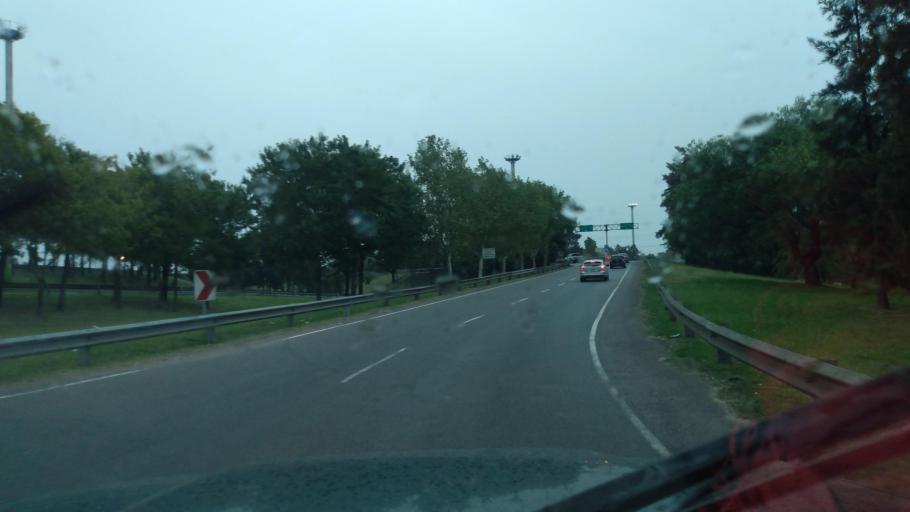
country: AR
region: Buenos Aires
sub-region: Partido de San Isidro
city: San Isidro
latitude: -34.4945
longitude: -58.5554
